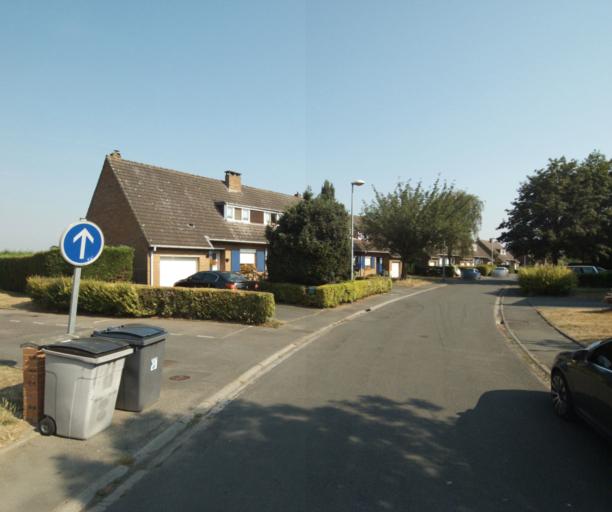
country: FR
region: Nord-Pas-de-Calais
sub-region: Departement du Nord
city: Quesnoy-sur-Deule
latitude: 50.7186
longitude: 2.9958
